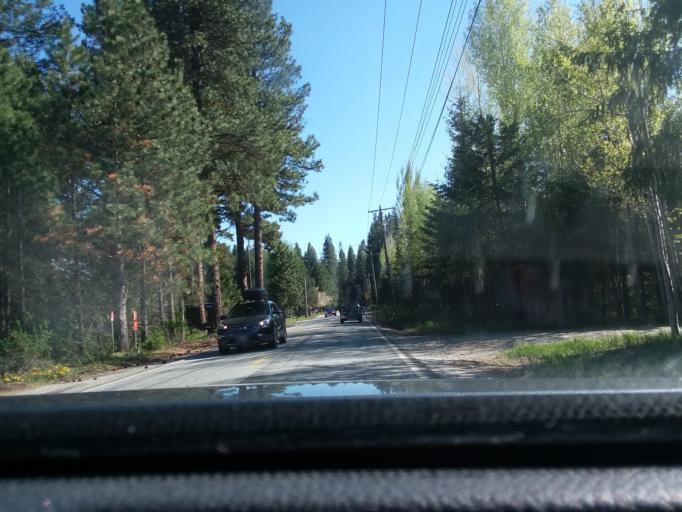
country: US
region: Washington
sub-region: Chelan County
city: Leavenworth
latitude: 47.7780
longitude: -120.6680
